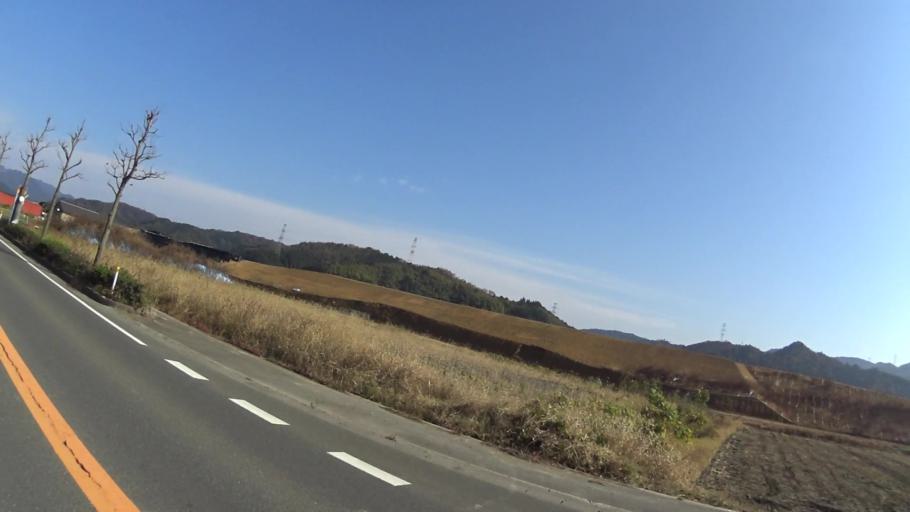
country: JP
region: Kyoto
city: Maizuru
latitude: 35.4340
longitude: 135.2531
